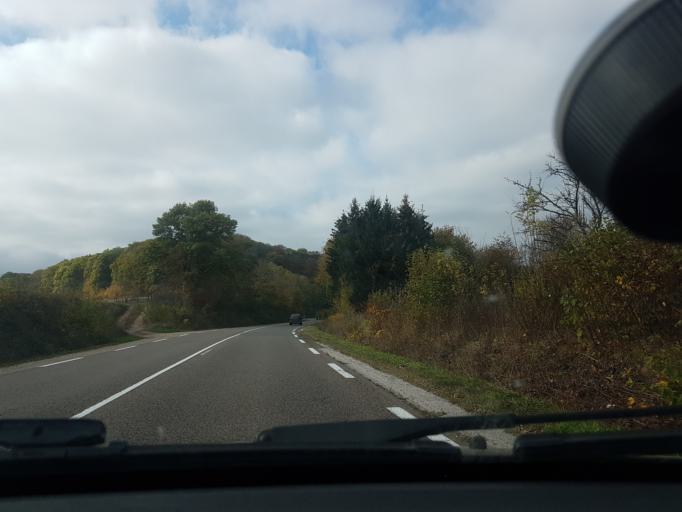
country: FR
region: Franche-Comte
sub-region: Departement de la Haute-Saone
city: Chalonvillars
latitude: 47.6502
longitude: 6.7647
